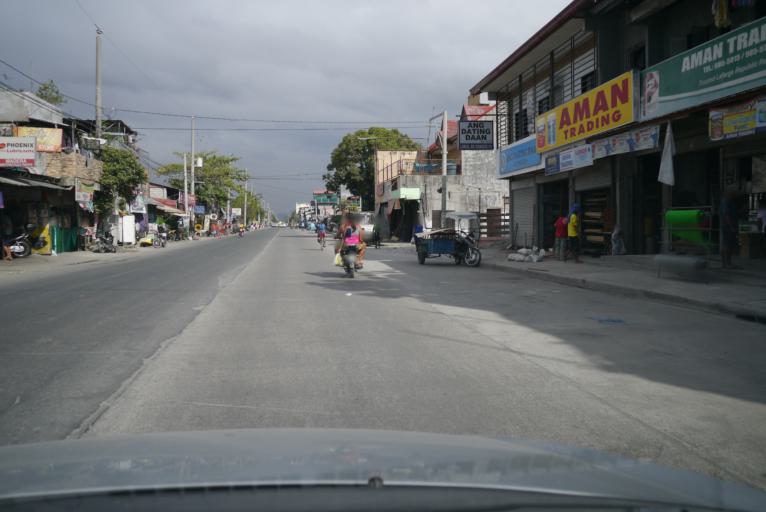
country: PH
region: Calabarzon
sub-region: Province of Rizal
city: Taytay
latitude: 14.5443
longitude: 121.1242
